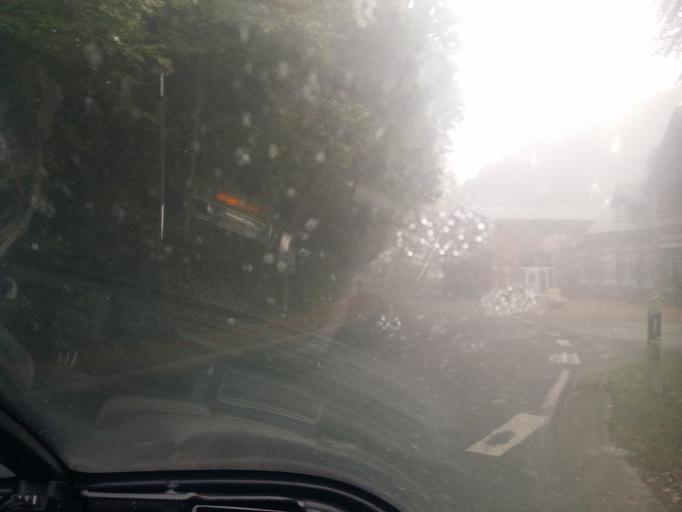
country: DE
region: Schleswig-Holstein
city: Drelsdorf
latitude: 54.6051
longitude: 9.0369
